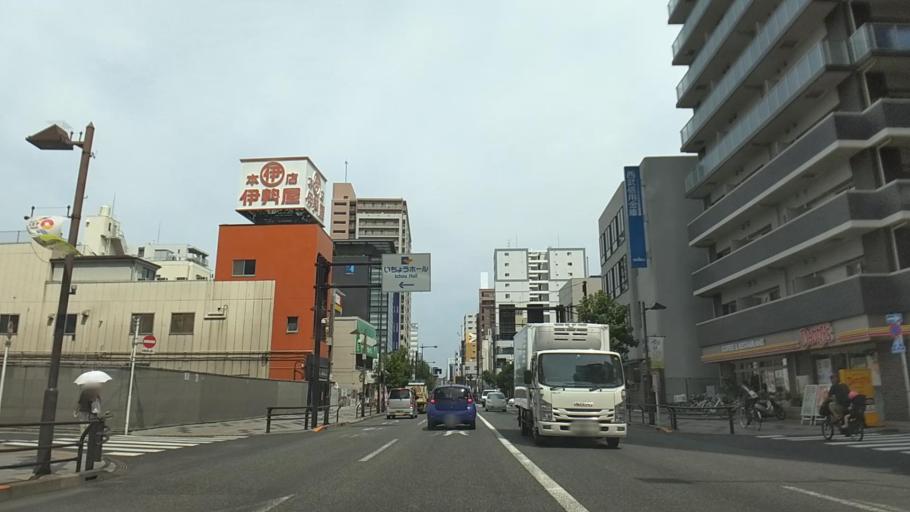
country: JP
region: Tokyo
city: Hachioji
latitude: 35.6600
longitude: 139.3324
